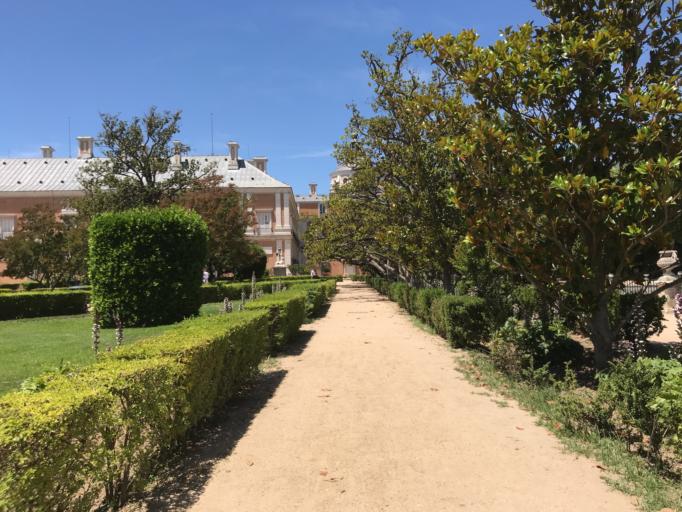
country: ES
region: Madrid
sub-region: Provincia de Madrid
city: Aranjuez
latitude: 40.0366
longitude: -3.6066
